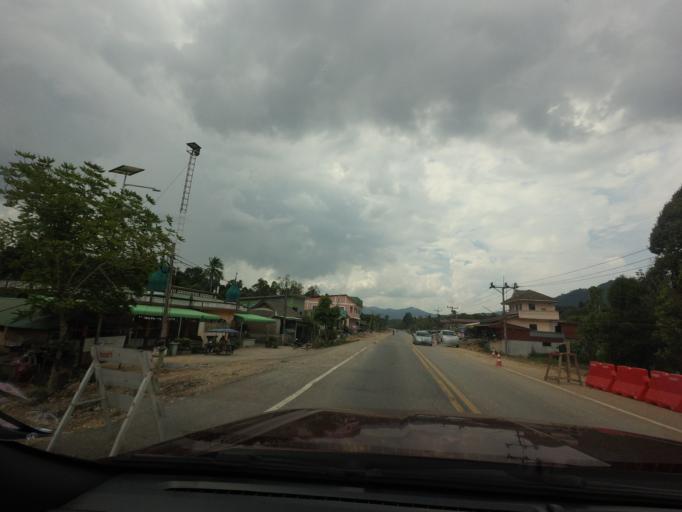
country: TH
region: Yala
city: Ban Nang Sata
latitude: 6.3054
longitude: 101.3020
